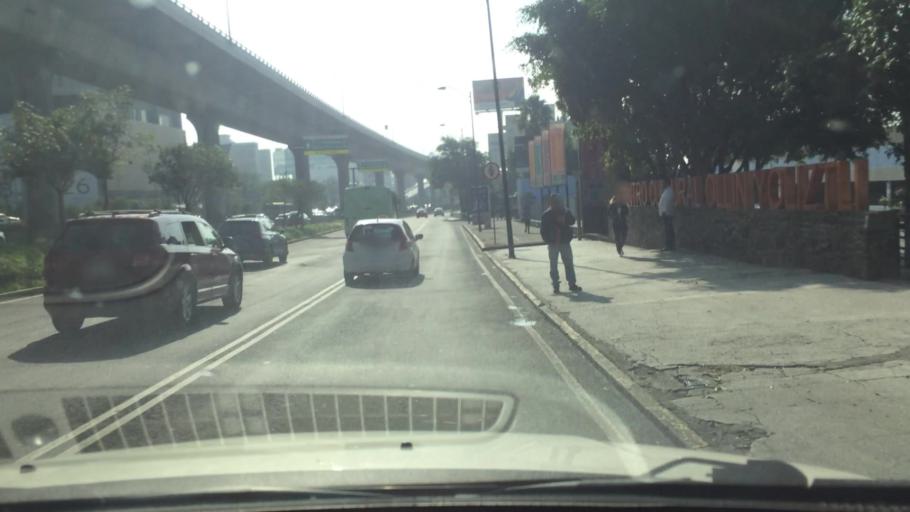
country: MX
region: Mexico City
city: Tlalpan
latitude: 19.3032
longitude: -99.1788
